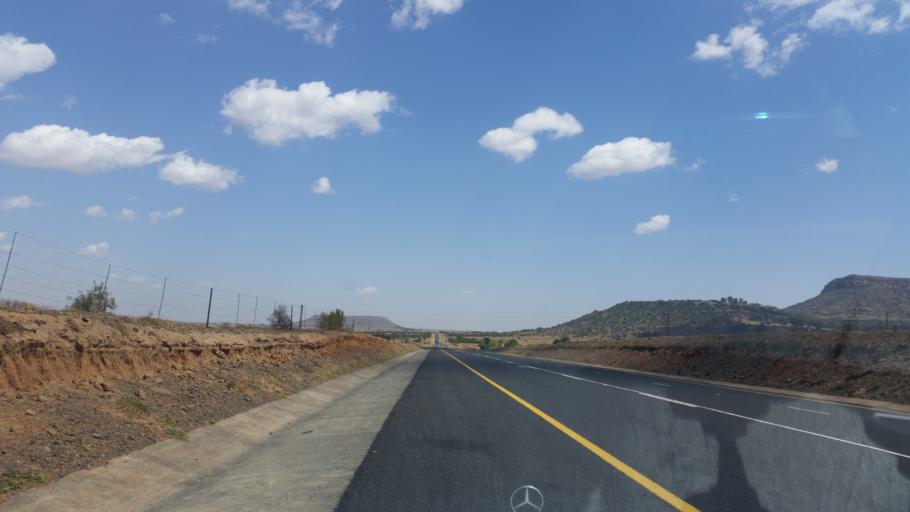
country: ZA
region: Orange Free State
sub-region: Thabo Mofutsanyana District Municipality
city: Senekal
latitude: -28.3015
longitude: 27.7912
